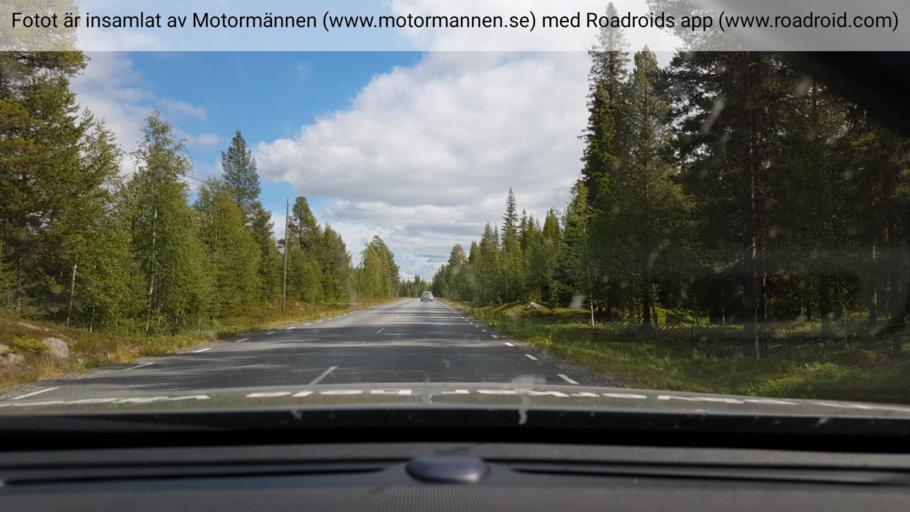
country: SE
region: Vaesterbotten
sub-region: Sorsele Kommun
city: Sorsele
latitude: 65.6655
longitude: 17.4003
